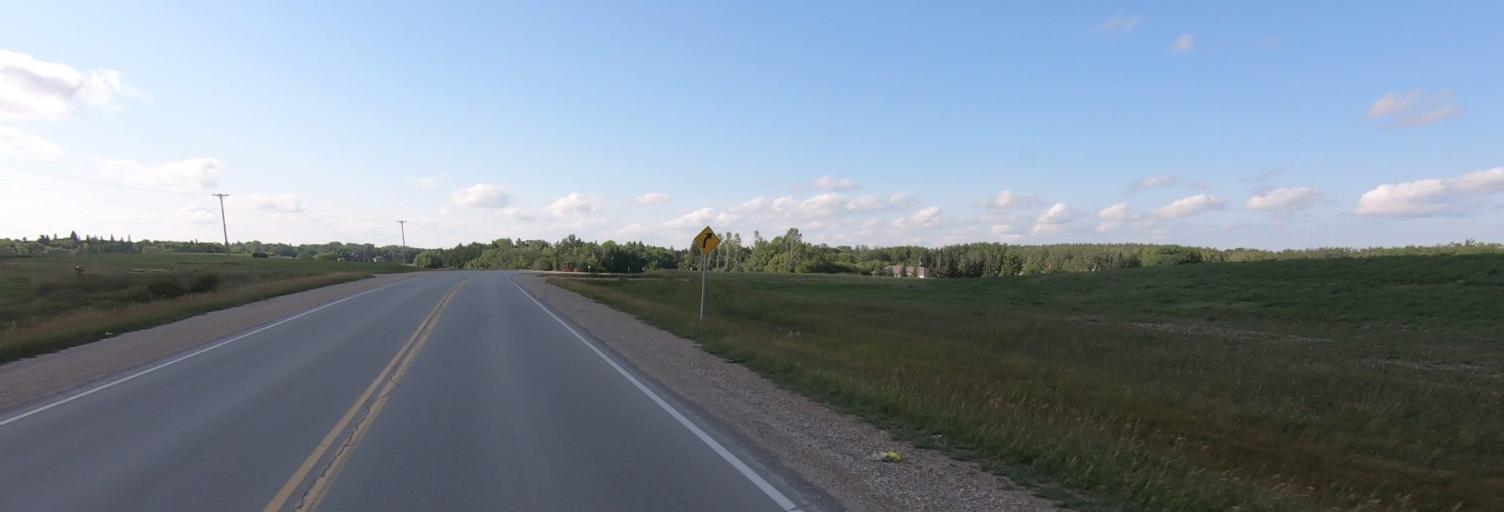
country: CA
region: Manitoba
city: Selkirk
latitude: 50.0911
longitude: -96.9299
